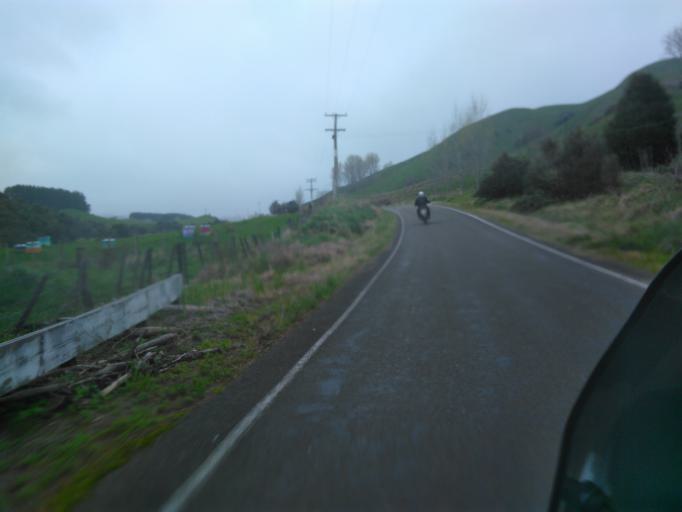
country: NZ
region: Gisborne
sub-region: Gisborne District
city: Gisborne
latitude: -38.6465
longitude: 177.7119
